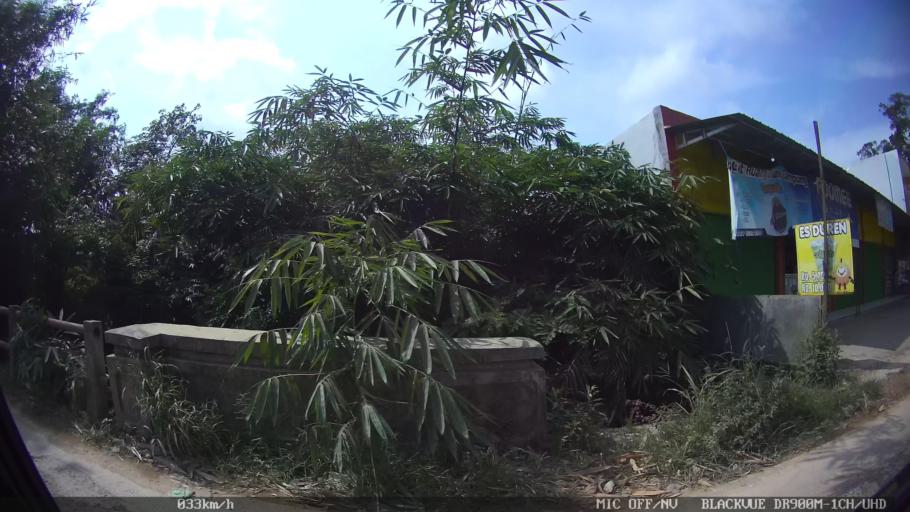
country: ID
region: Lampung
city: Kedaton
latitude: -5.3404
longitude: 105.2729
